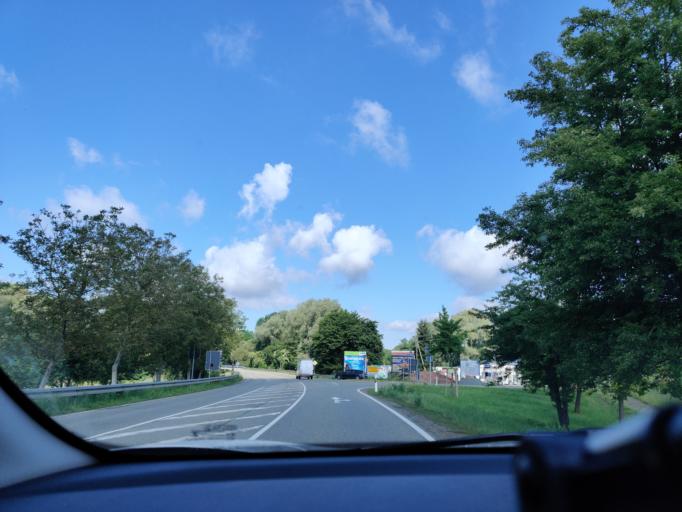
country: FR
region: Lorraine
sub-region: Departement de la Moselle
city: Sarreinsming
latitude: 49.1391
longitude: 7.1314
